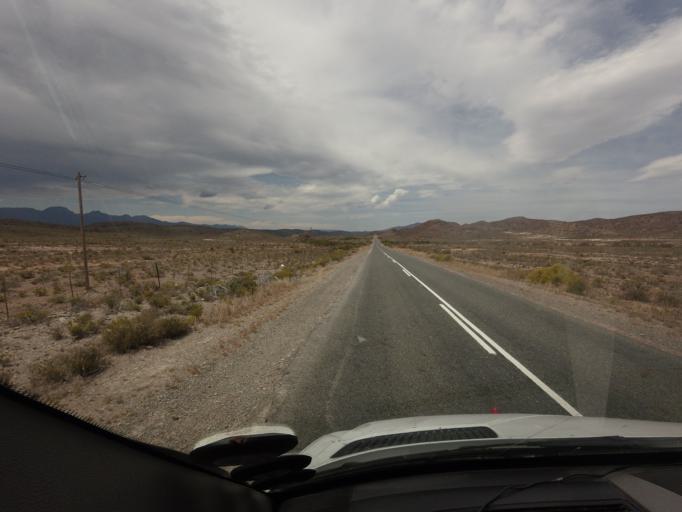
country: ZA
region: Western Cape
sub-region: Eden District Municipality
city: Ladismith
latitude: -33.5996
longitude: 21.1014
